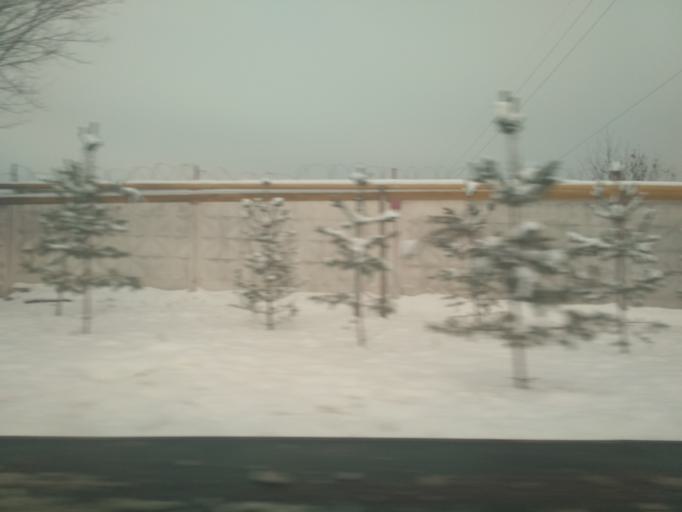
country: KZ
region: Almaty Qalasy
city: Almaty
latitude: 43.2259
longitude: 76.7974
